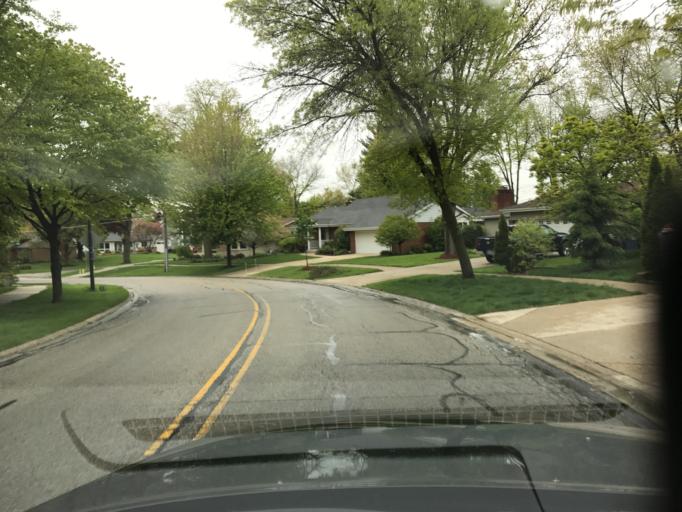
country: US
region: Illinois
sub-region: DuPage County
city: Naperville
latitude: 41.7663
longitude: -88.1386
